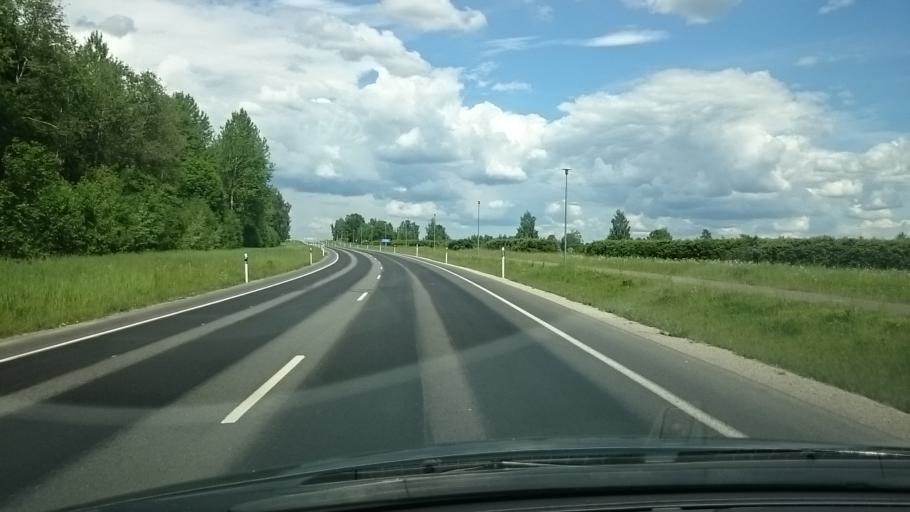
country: EE
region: Jaervamaa
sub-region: Tueri vald
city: Tueri
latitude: 58.8328
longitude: 25.4692
